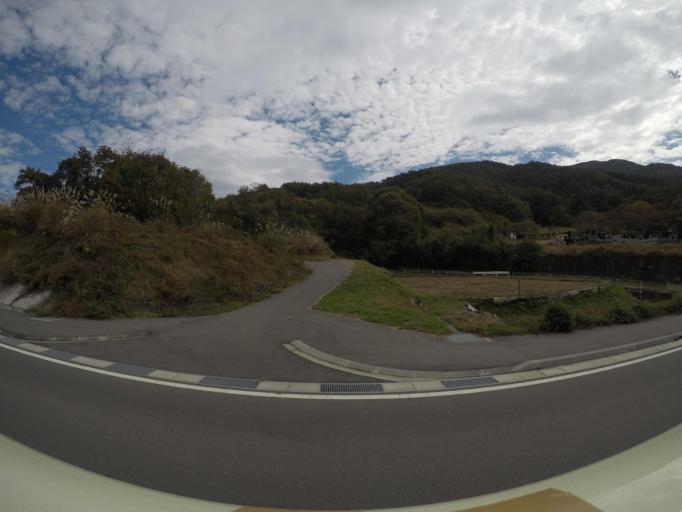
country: JP
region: Nagano
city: Chino
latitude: 35.8870
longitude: 138.0971
